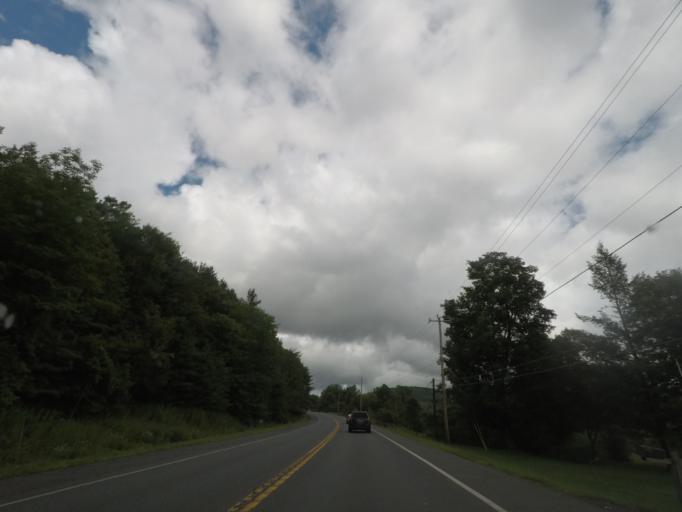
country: US
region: Massachusetts
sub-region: Berkshire County
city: Williamstown
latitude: 42.6810
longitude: -73.3665
